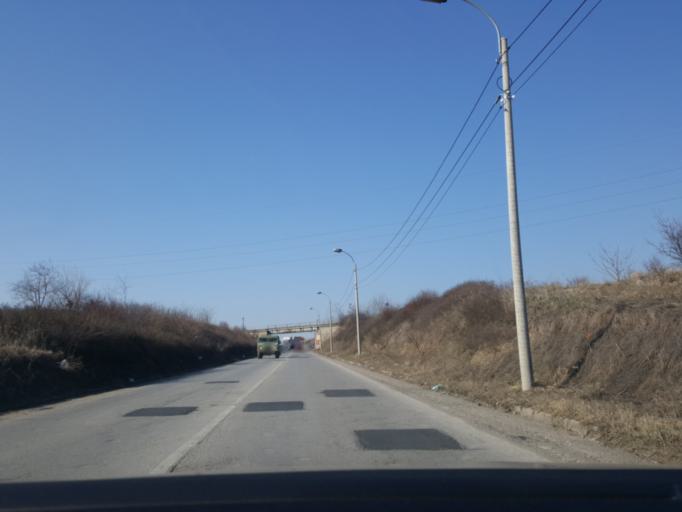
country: RS
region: Central Serbia
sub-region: Nisavski Okrug
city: Nis
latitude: 43.3404
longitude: 21.8859
